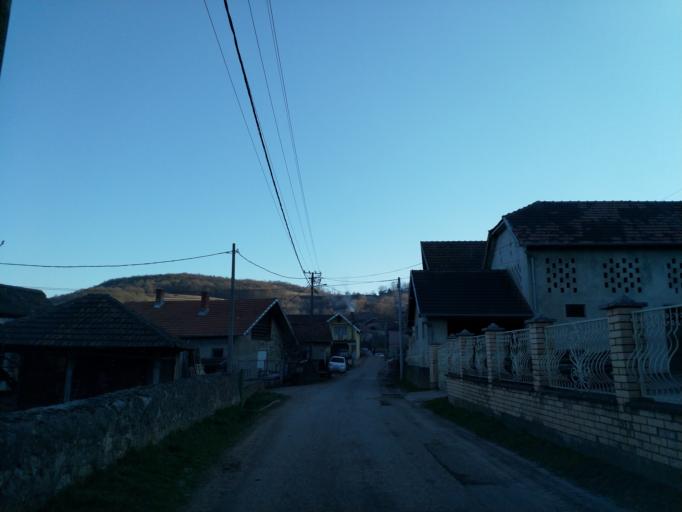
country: RS
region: Central Serbia
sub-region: Pomoravski Okrug
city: Paracin
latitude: 43.9313
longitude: 21.5193
